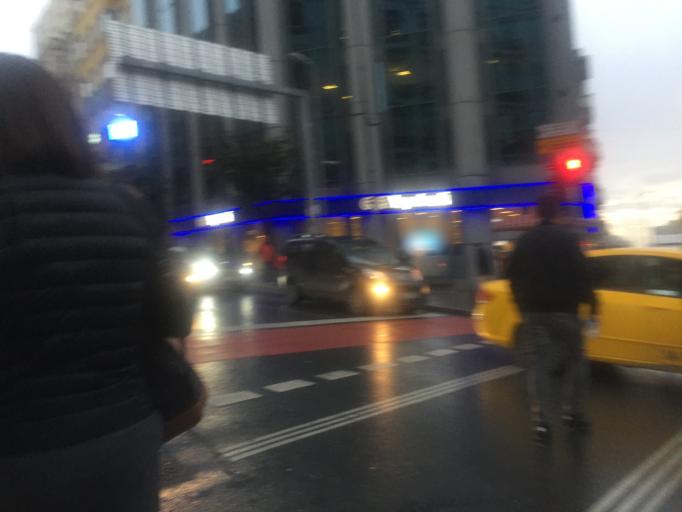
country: TR
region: Istanbul
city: Sisli
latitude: 41.0536
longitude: 28.9873
